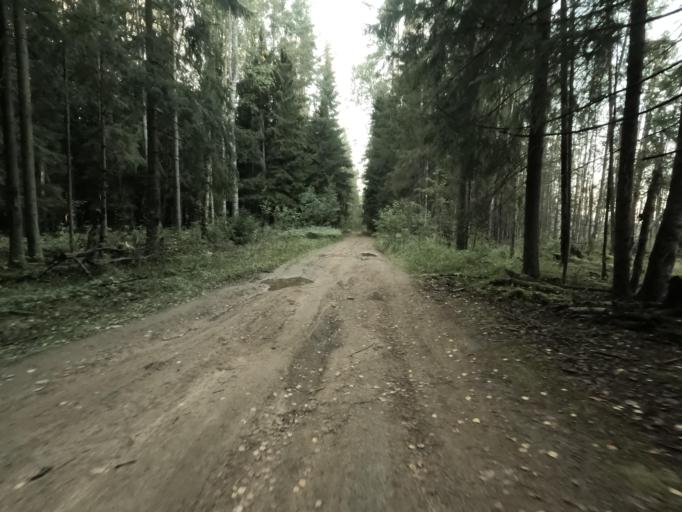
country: RU
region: Leningrad
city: Otradnoye
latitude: 59.8365
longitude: 30.8069
